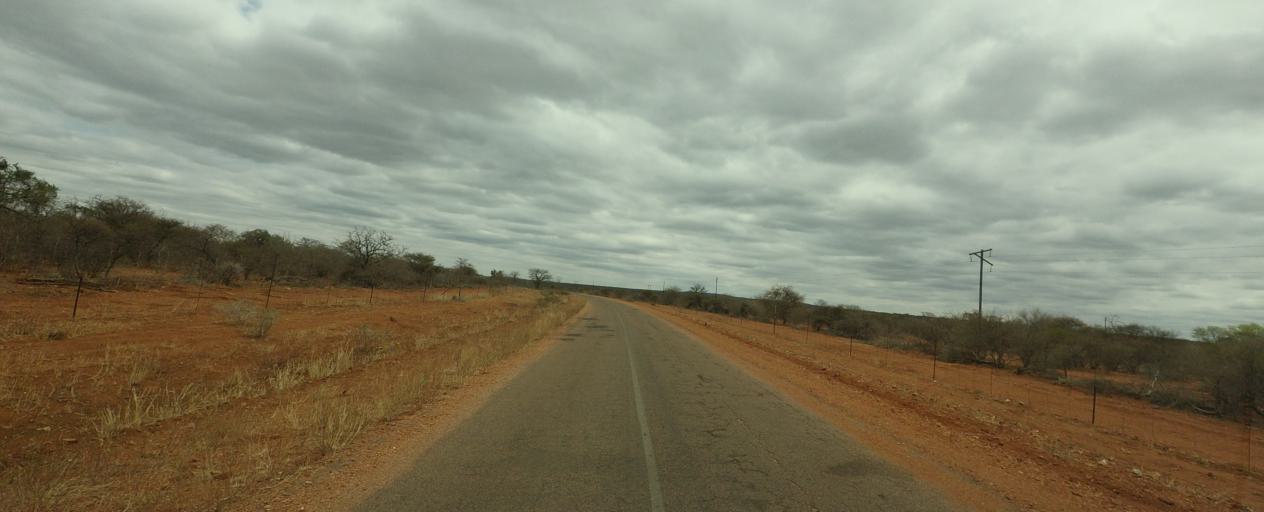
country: BW
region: Central
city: Mathathane
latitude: -22.7393
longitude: 28.4572
